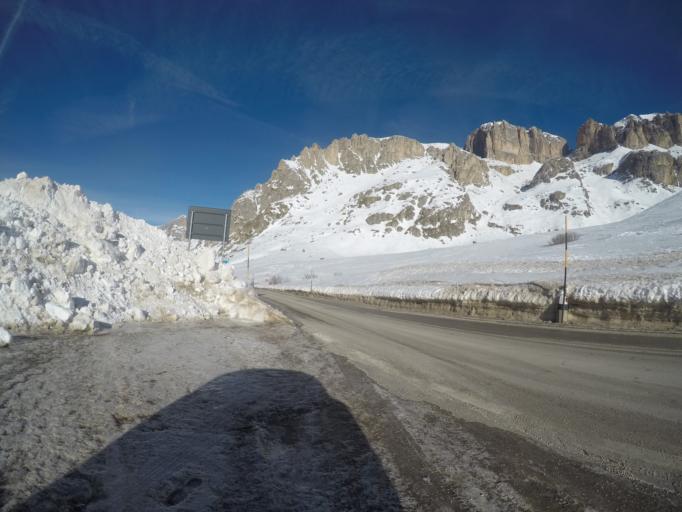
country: IT
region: Trentino-Alto Adige
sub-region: Provincia di Trento
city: Canazei
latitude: 46.4885
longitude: 11.8098
